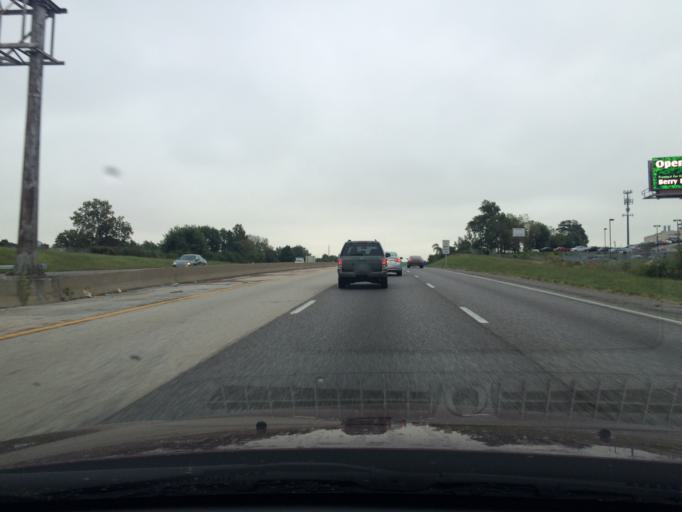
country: US
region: Missouri
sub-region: Saint Louis County
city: Bridgeton
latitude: 38.7440
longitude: -90.4099
